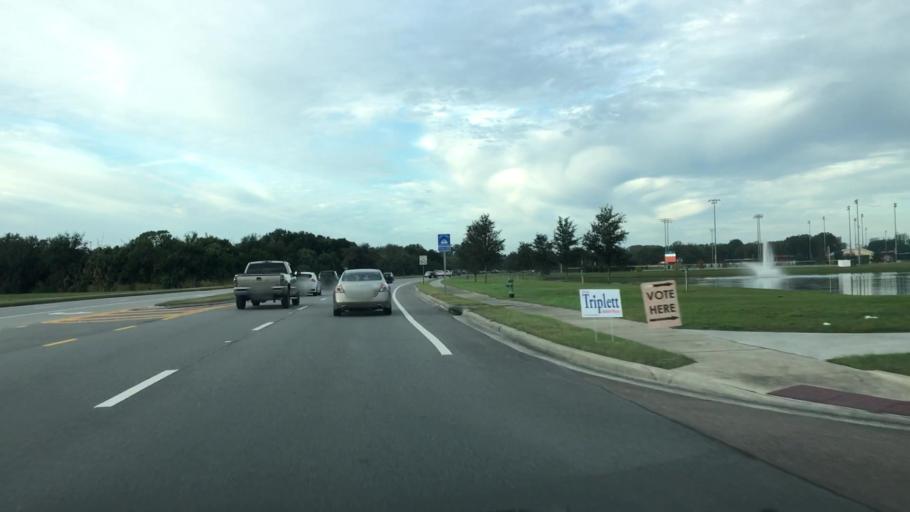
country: US
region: Florida
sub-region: Seminole County
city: Midway
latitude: 28.7627
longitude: -81.2144
